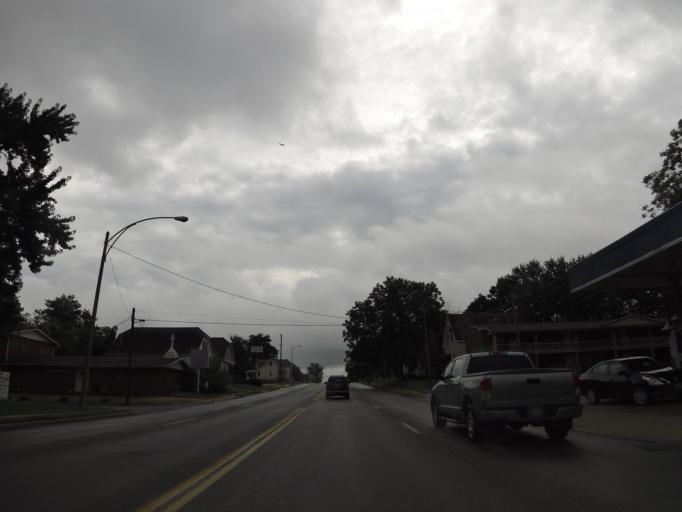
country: US
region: Missouri
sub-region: Cape Girardeau County
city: Cape Girardeau
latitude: 37.3017
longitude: -89.5336
